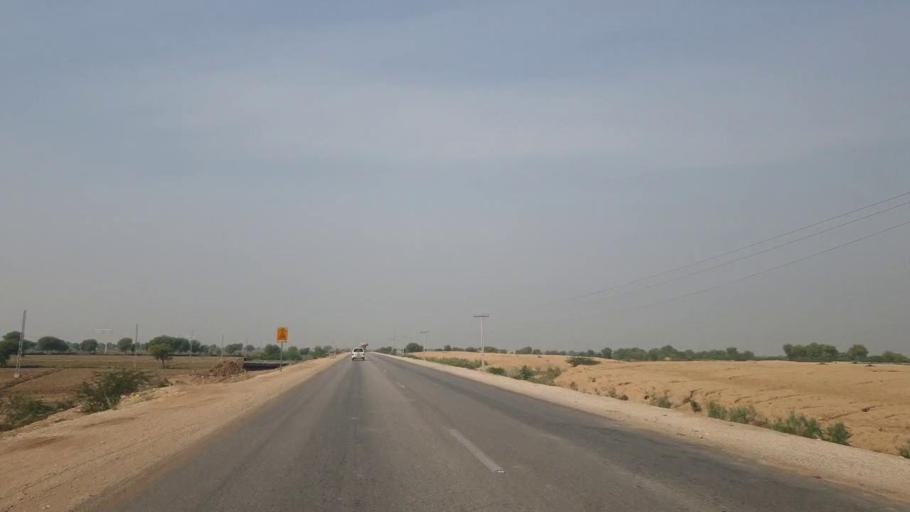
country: PK
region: Sindh
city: Sann
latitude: 26.0664
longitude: 68.1011
